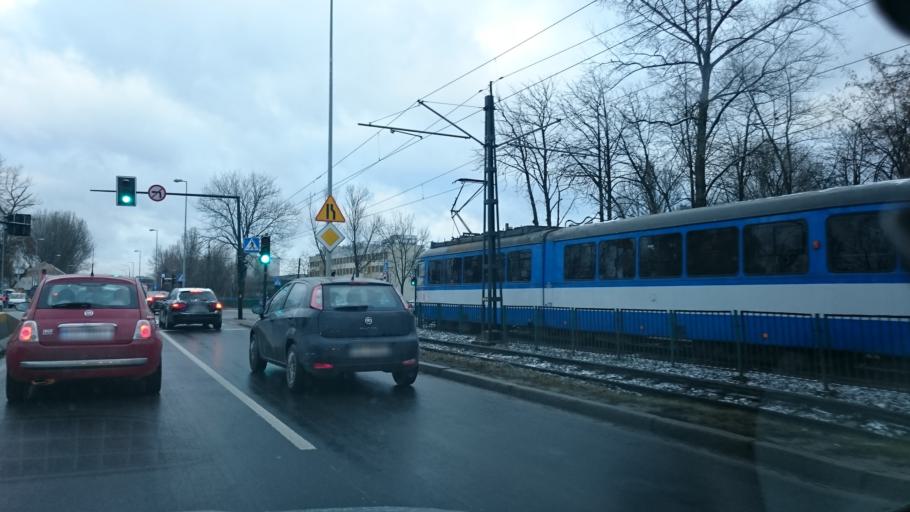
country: PL
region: Lesser Poland Voivodeship
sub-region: Krakow
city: Krakow
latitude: 50.0266
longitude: 19.9772
